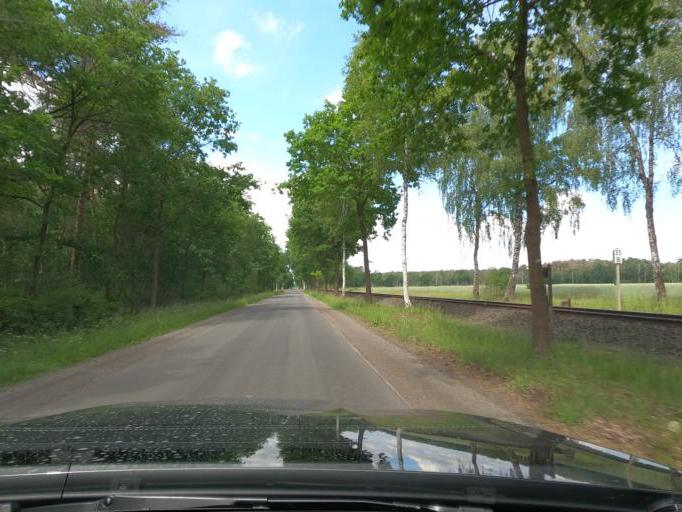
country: DE
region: Lower Saxony
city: Schwarmstedt
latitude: 52.6416
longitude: 9.6361
